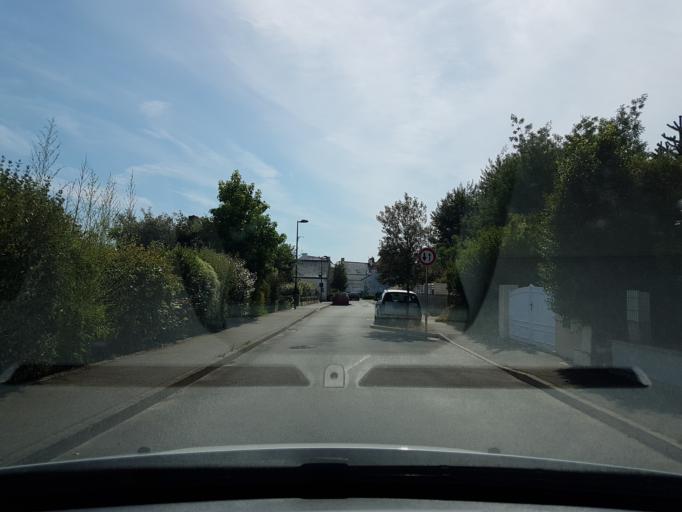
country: FR
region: Brittany
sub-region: Departement du Morbihan
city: Etel
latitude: 47.6784
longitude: -3.2078
